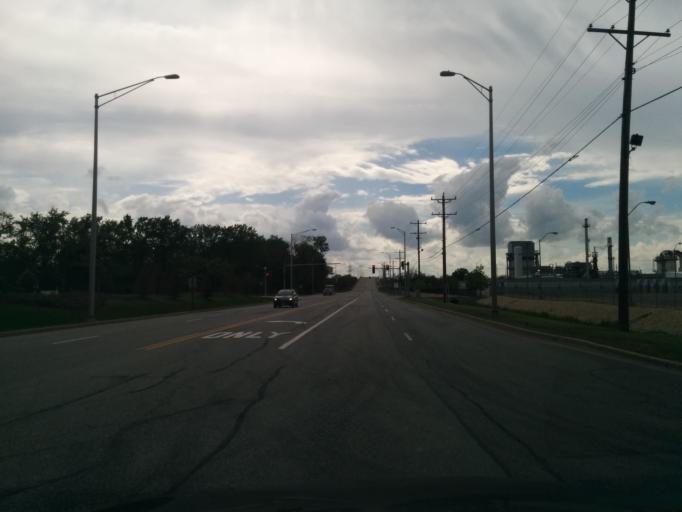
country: US
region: Illinois
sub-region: Will County
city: Romeoville
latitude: 41.6408
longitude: -88.0515
